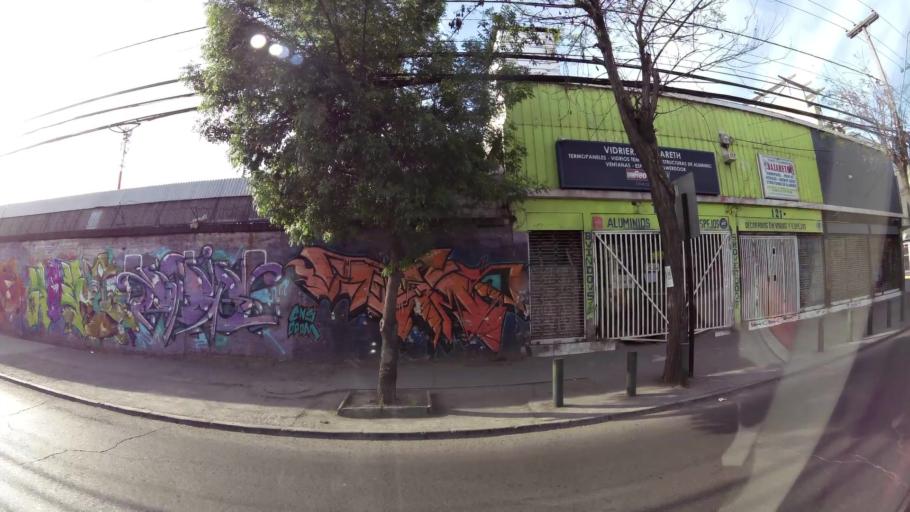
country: CL
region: Santiago Metropolitan
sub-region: Provincia de Cordillera
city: Puente Alto
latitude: -33.6126
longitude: -70.5773
